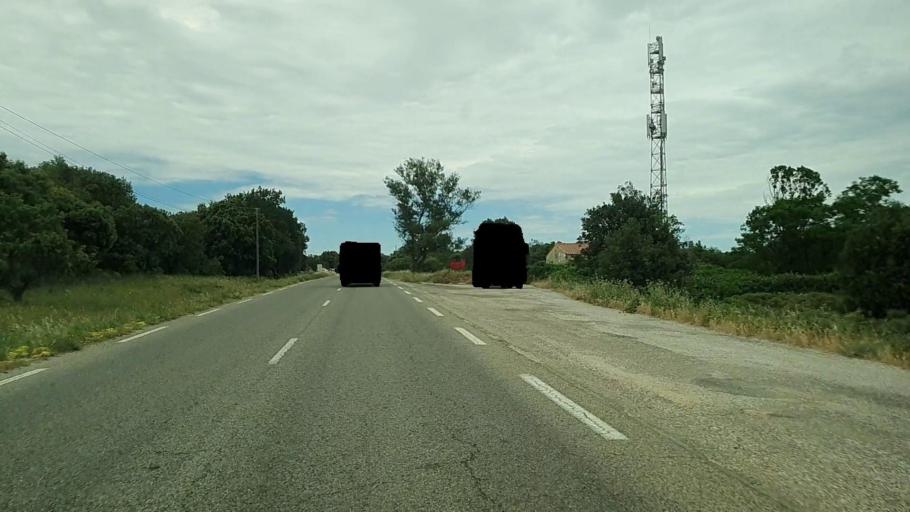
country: FR
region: Languedoc-Roussillon
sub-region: Departement du Gard
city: Connaux
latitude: 44.0511
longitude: 4.5727
